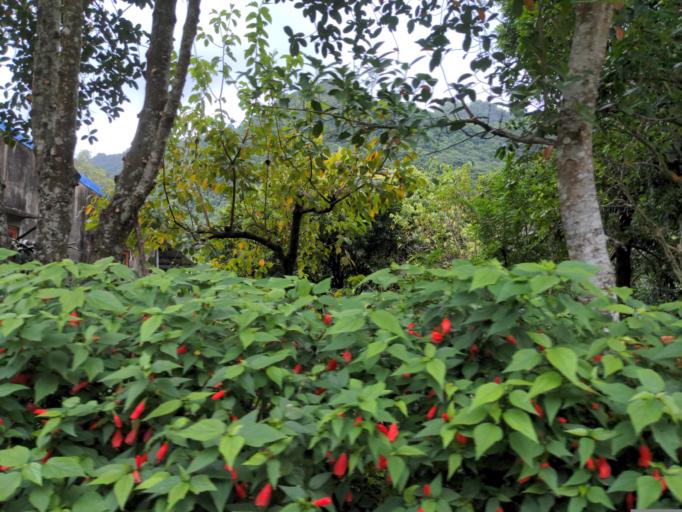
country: VN
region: Hai Phong
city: Cat Ba
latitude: 20.7988
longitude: 107.0425
